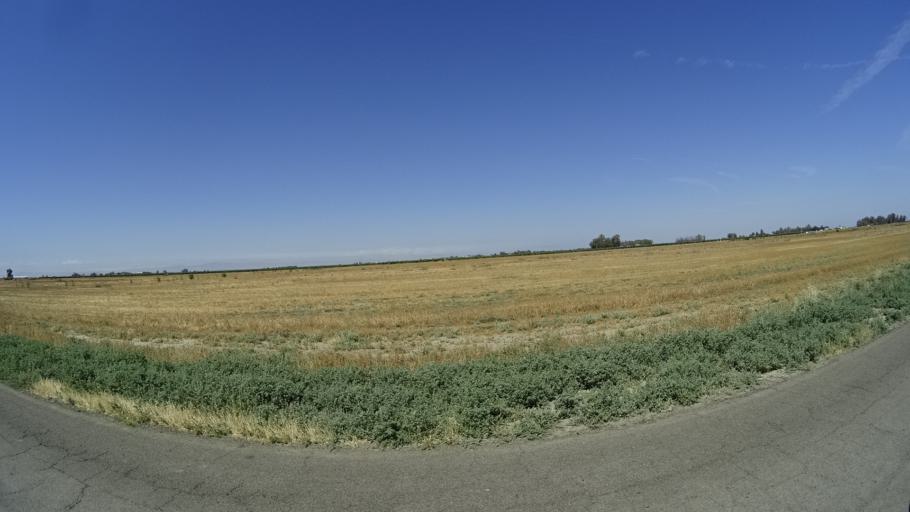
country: US
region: California
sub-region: Kings County
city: Stratford
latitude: 36.1862
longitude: -119.7803
